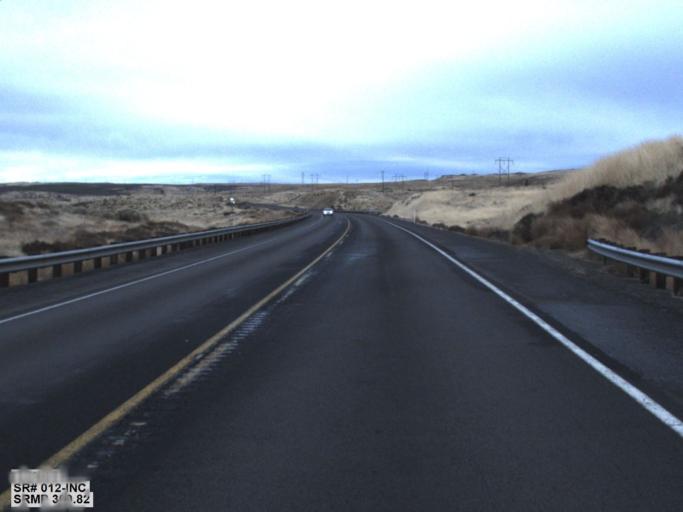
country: US
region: Washington
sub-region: Benton County
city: Finley
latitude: 46.0544
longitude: -118.8633
